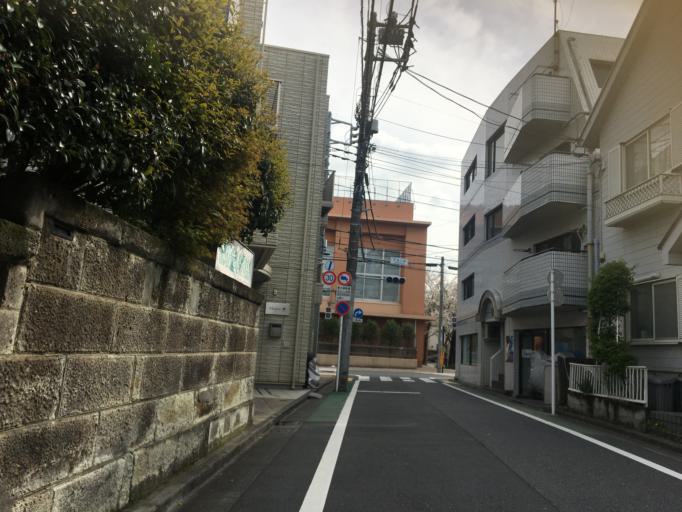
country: JP
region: Tokyo
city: Musashino
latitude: 35.7113
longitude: 139.6229
